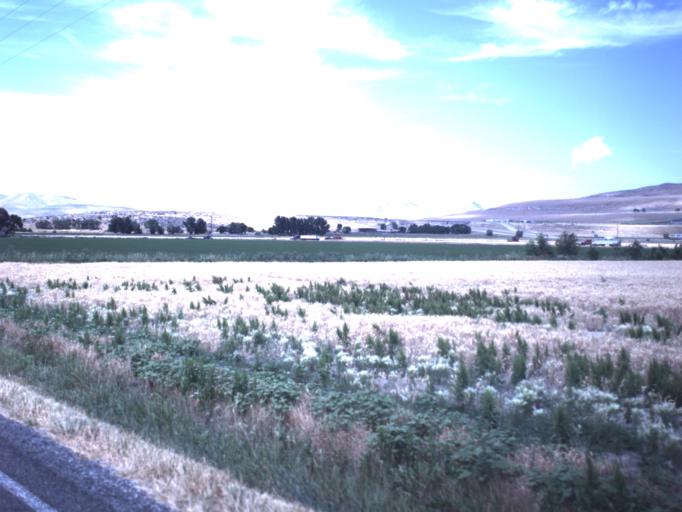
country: US
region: Utah
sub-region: Box Elder County
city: Tremonton
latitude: 41.7107
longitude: -112.2139
